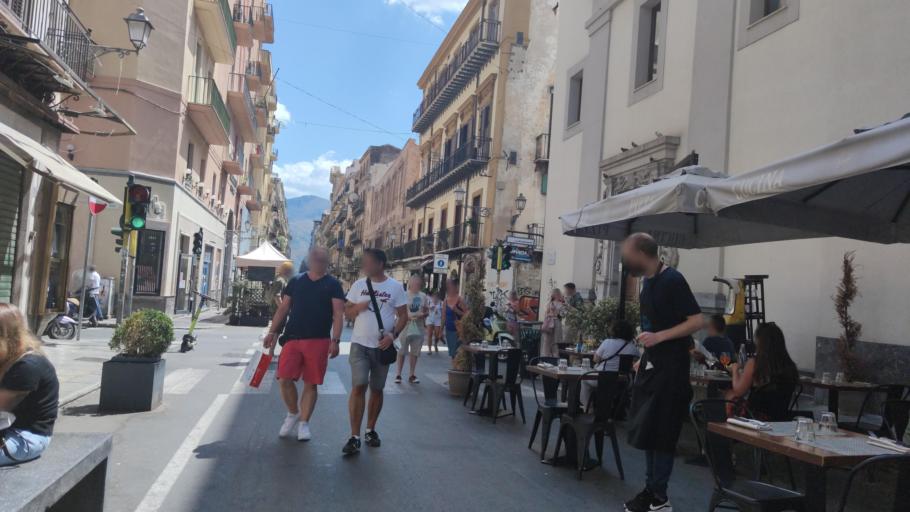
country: IT
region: Sicily
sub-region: Palermo
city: Palermo
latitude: 38.1180
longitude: 13.3600
